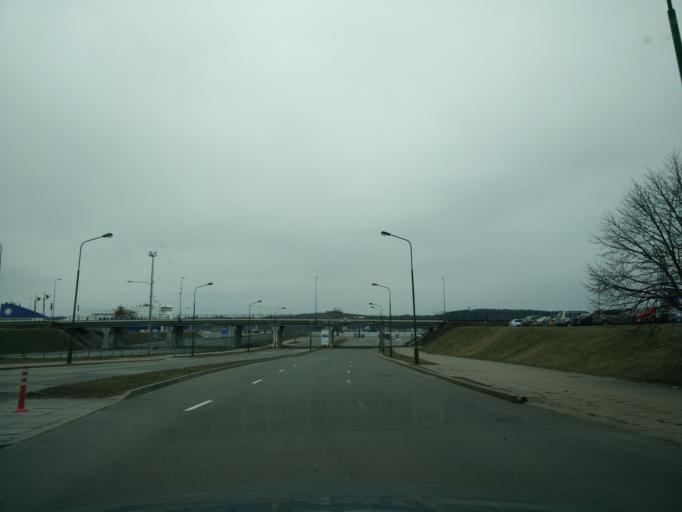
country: LT
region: Klaipedos apskritis
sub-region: Klaipeda
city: Klaipeda
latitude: 55.6887
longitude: 21.1430
